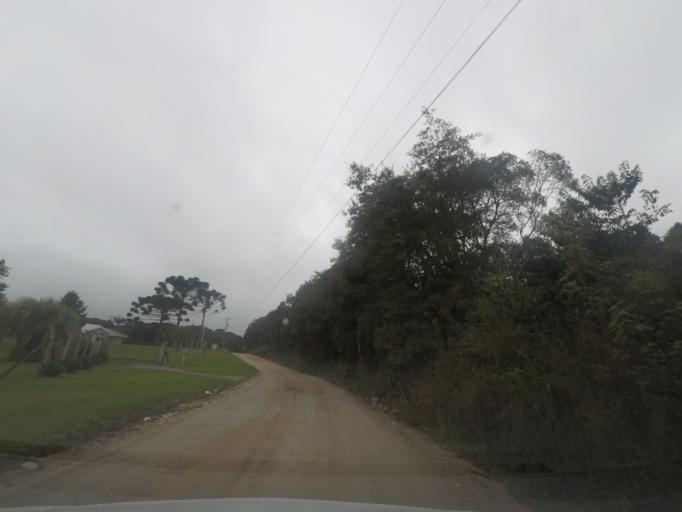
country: BR
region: Parana
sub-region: Campina Grande Do Sul
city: Campina Grande do Sul
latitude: -25.3092
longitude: -49.1019
